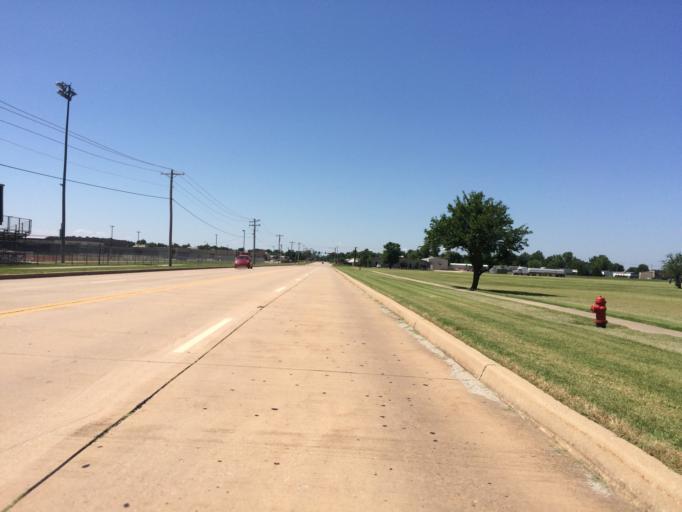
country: US
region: Oklahoma
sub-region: Cleveland County
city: Norman
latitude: 35.2448
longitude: -97.4501
